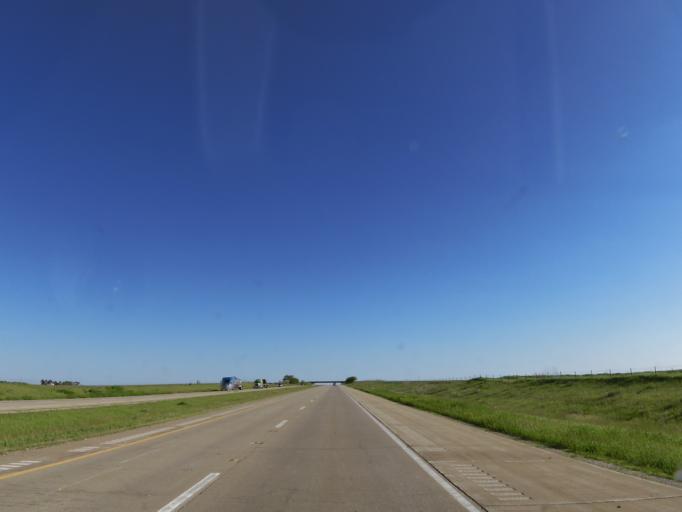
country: US
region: Illinois
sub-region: Woodford County
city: El Paso
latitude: 40.7958
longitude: -89.0356
